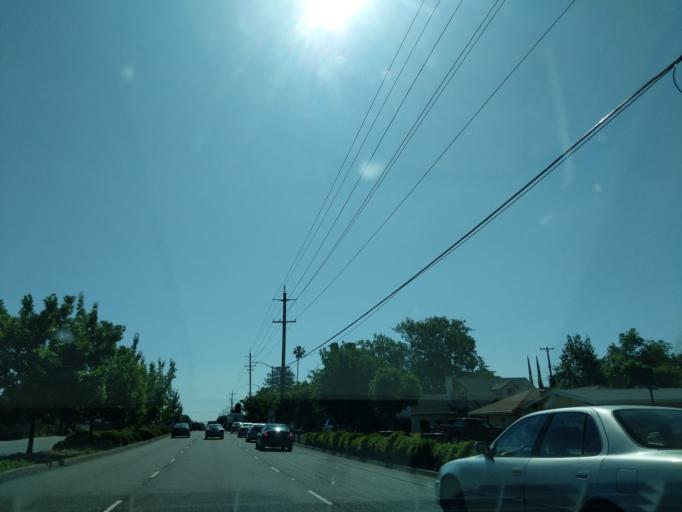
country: US
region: California
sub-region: Sacramento County
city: Citrus Heights
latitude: 38.6782
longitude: -121.3019
